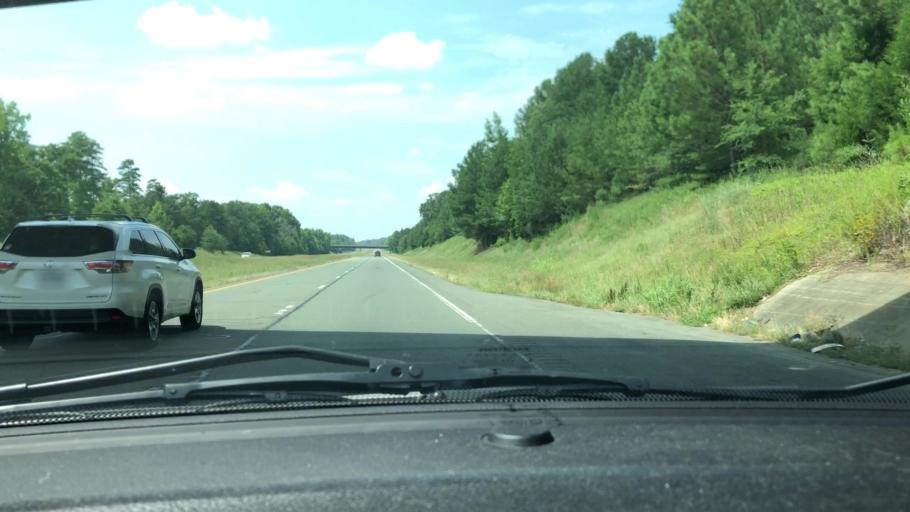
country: US
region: North Carolina
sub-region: Randolph County
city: Liberty
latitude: 35.7975
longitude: -79.5345
